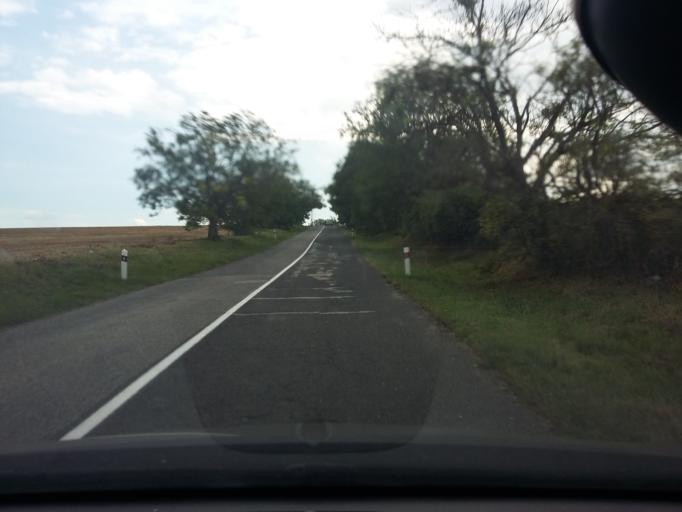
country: SK
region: Trnavsky
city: Gbely
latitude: 48.6655
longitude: 17.1478
